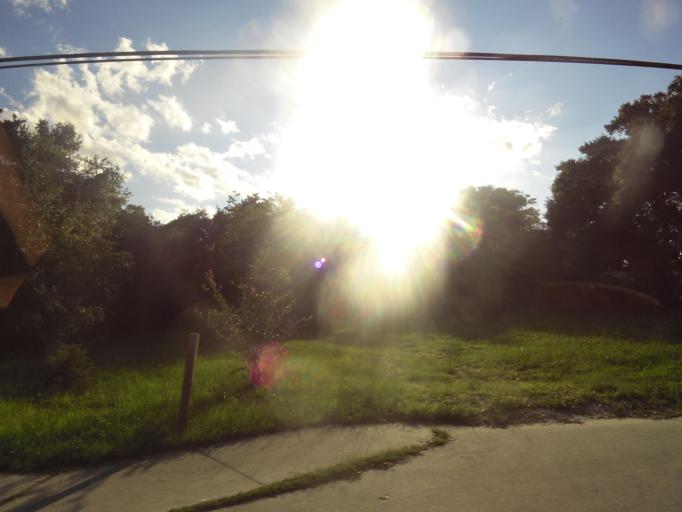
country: US
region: Florida
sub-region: Nassau County
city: Fernandina Beach
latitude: 30.6662
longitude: -81.4521
